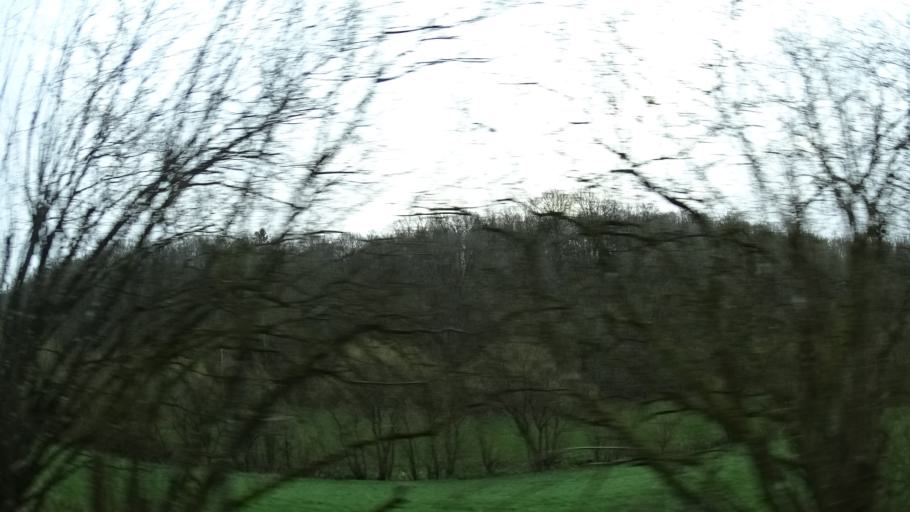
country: DE
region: Rheinland-Pfalz
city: Dienstweiler
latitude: 49.6469
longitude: 7.1970
